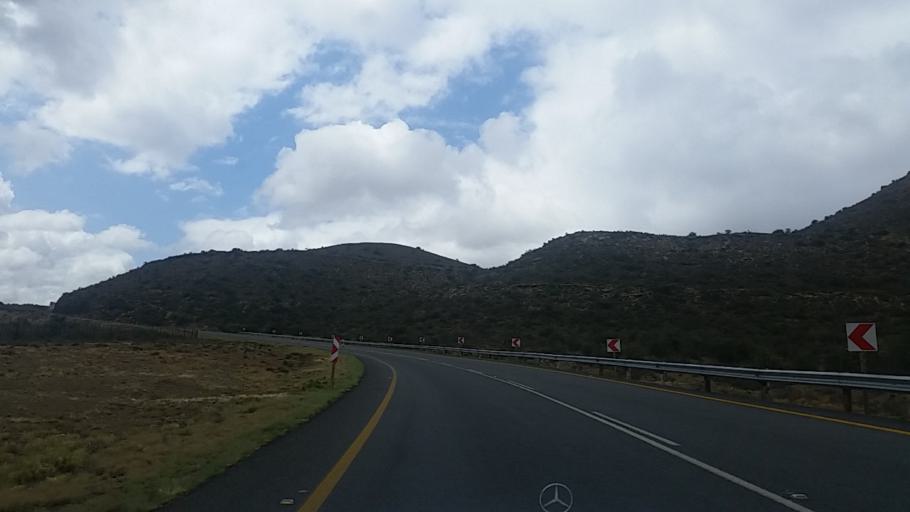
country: ZA
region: Eastern Cape
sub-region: Cacadu District Municipality
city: Graaff-Reinet
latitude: -32.1182
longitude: 24.6078
